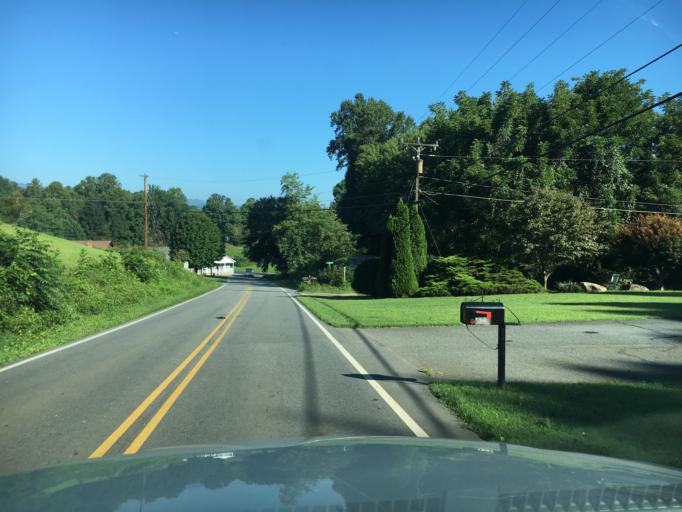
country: US
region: North Carolina
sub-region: McDowell County
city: West Marion
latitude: 35.6585
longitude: -82.0337
